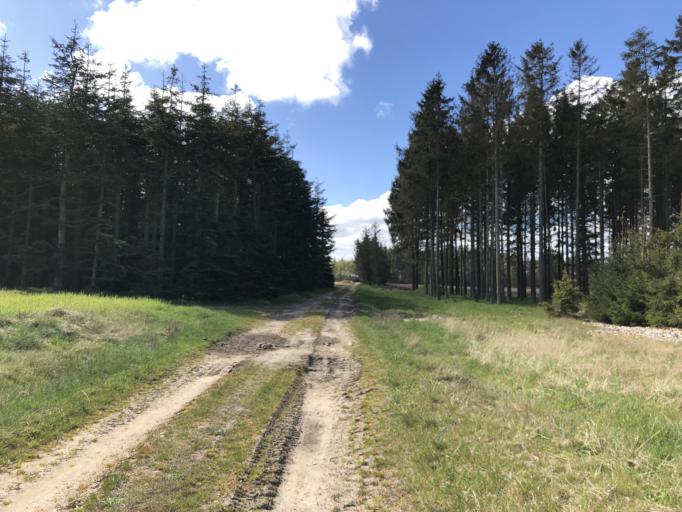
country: DK
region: Central Jutland
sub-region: Holstebro Kommune
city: Ulfborg
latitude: 56.2422
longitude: 8.4685
